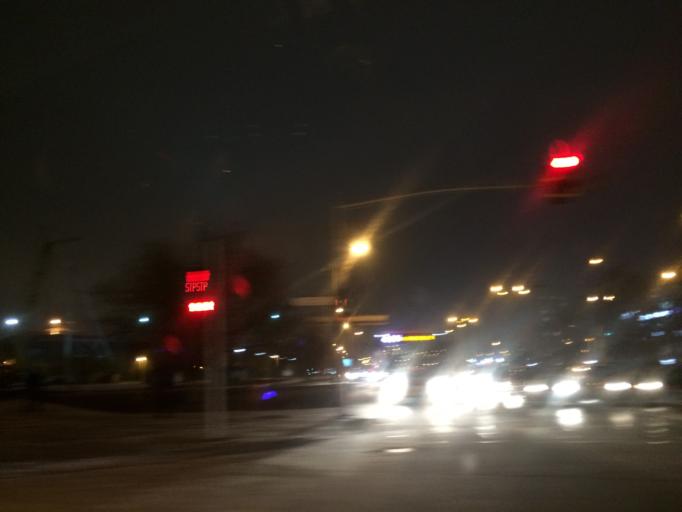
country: KZ
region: Astana Qalasy
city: Astana
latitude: 51.1461
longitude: 71.4122
